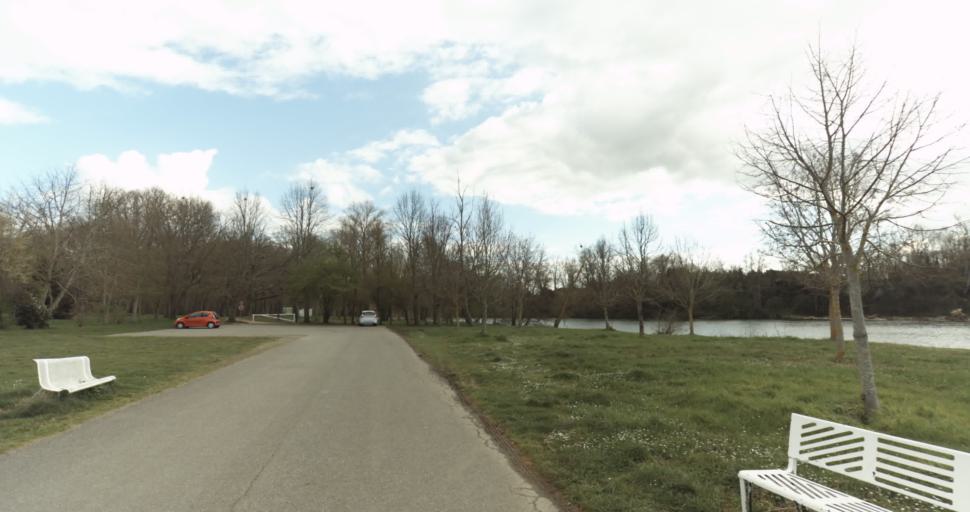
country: FR
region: Midi-Pyrenees
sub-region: Departement de la Haute-Garonne
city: Auterive
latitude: 43.3386
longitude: 1.4837
